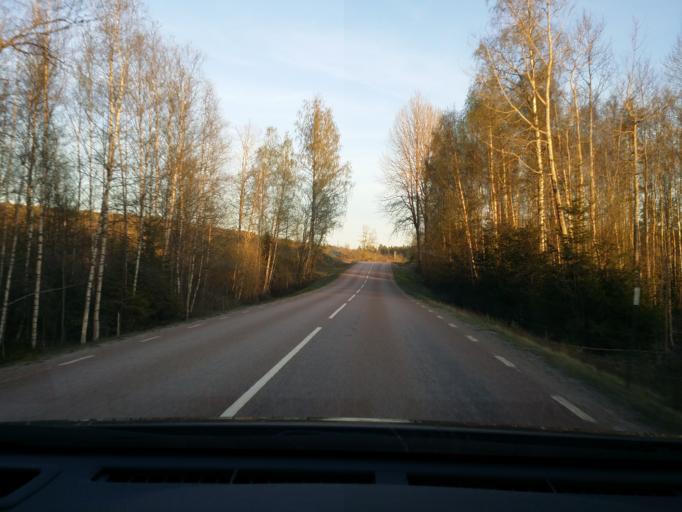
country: SE
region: Vaestmanland
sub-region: Sala Kommun
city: Sala
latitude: 59.8069
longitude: 16.5504
